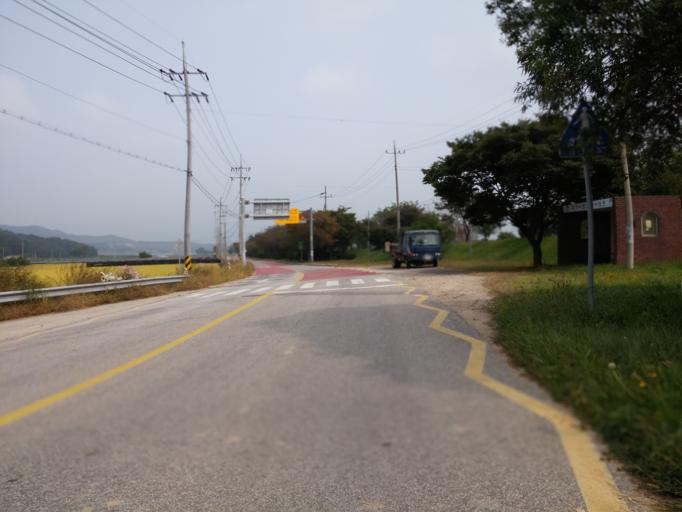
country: KR
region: Chungcheongbuk-do
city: Okcheon
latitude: 36.4216
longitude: 127.7750
